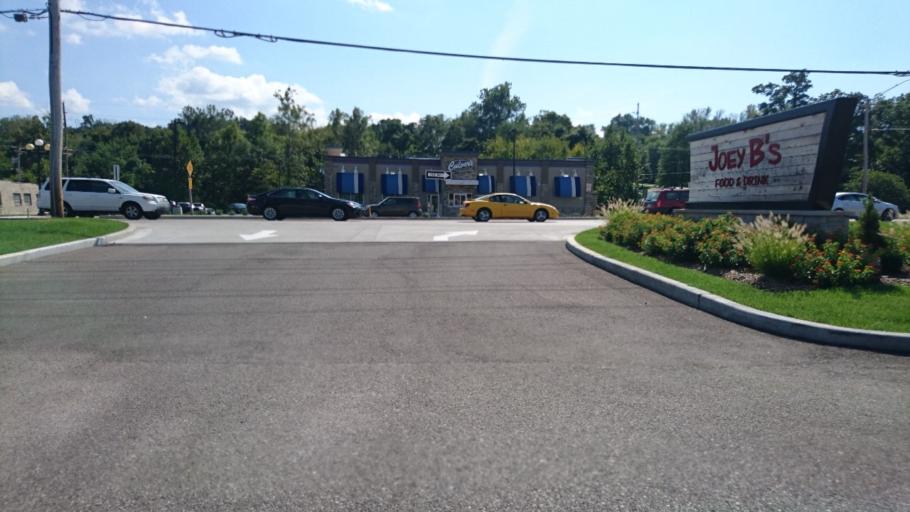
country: US
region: Missouri
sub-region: Saint Louis County
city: Winchester
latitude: 38.5936
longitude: -90.5193
